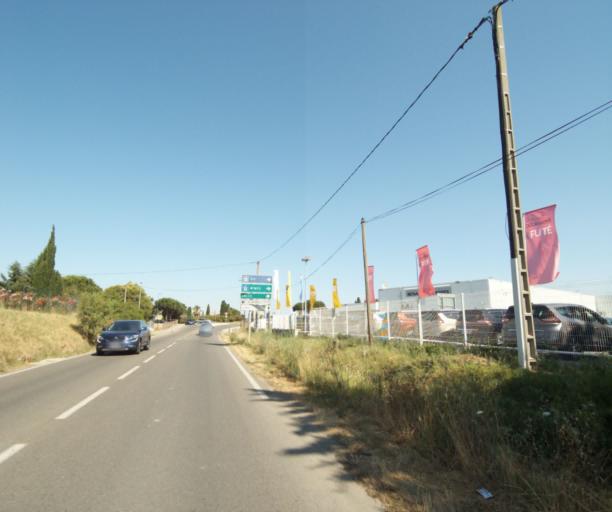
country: FR
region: Languedoc-Roussillon
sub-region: Departement de l'Herault
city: Lunel
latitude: 43.6719
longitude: 4.1487
